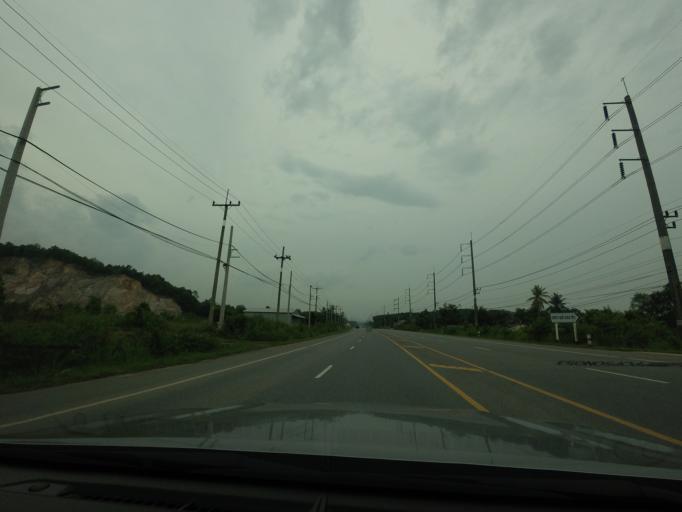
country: TH
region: Songkhla
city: Na Mom
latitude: 7.0256
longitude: 100.6646
